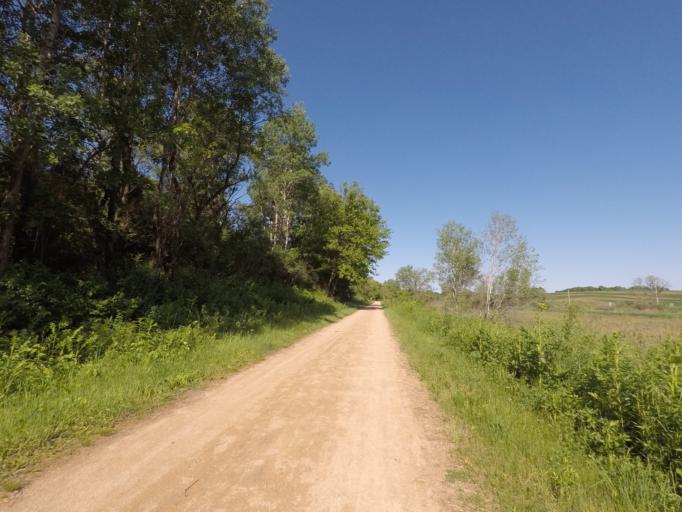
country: US
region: Wisconsin
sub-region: Dane County
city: Cross Plains
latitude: 43.0272
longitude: -89.6395
